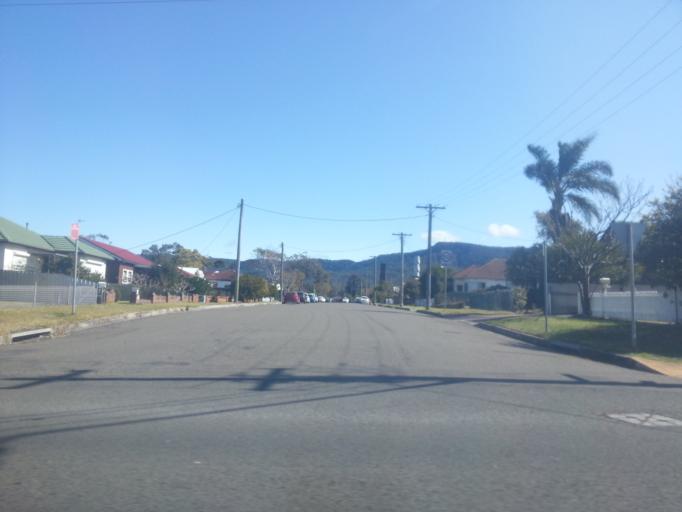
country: AU
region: New South Wales
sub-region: Wollongong
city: East Corrimal
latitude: -34.3799
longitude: 150.9079
